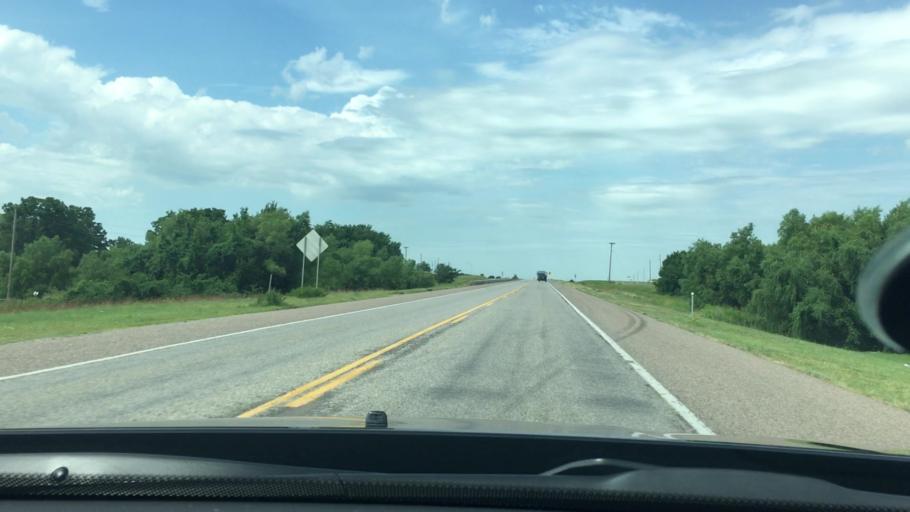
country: US
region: Oklahoma
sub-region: Pontotoc County
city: Ada
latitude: 34.6634
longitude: -96.7900
